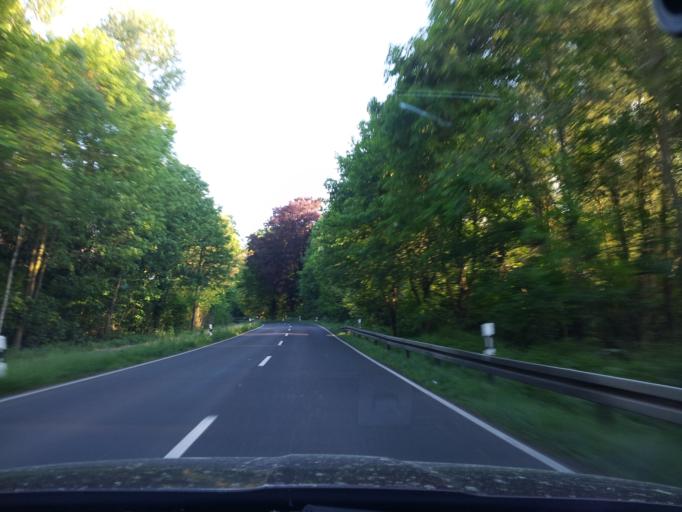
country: DE
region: Brandenburg
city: Luckenwalde
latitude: 52.0658
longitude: 13.1556
